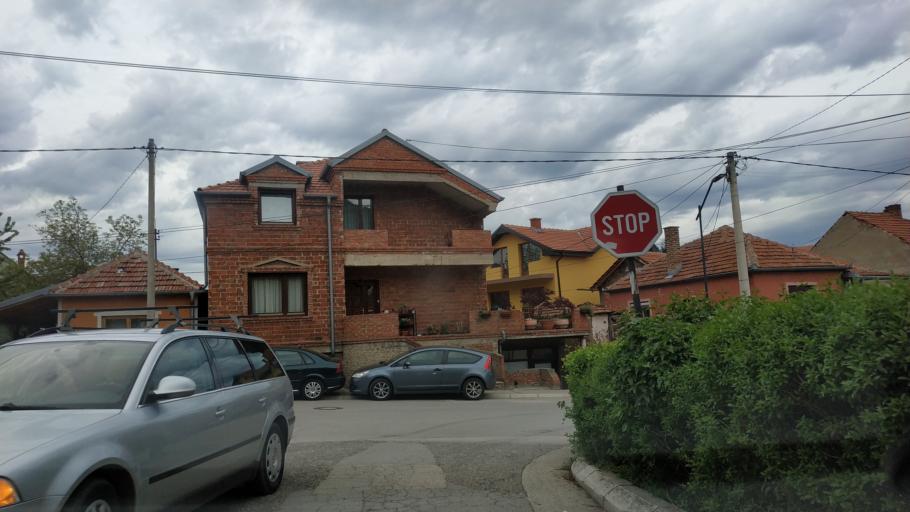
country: RS
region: Central Serbia
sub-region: Zajecarski Okrug
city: Soko Banja
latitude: 43.6432
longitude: 21.8678
